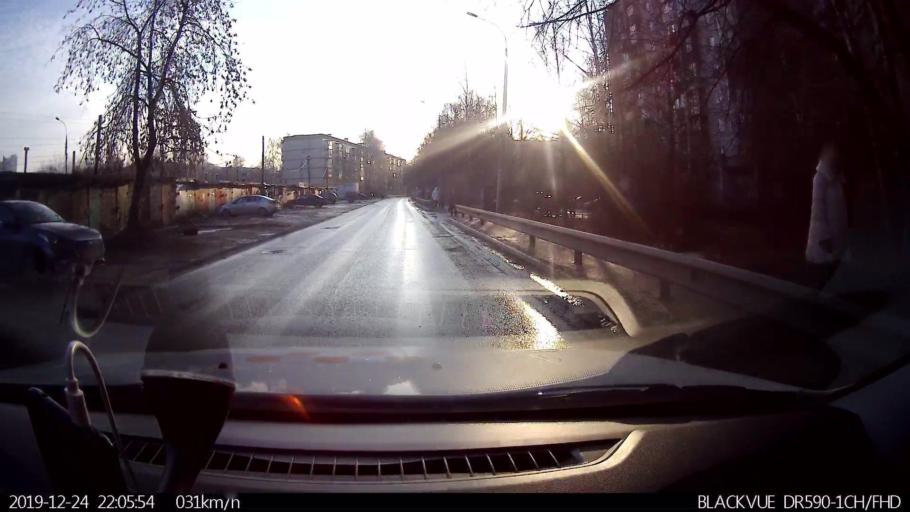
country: RU
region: Nizjnij Novgorod
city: Nizhniy Novgorod
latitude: 56.3184
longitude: 43.8819
